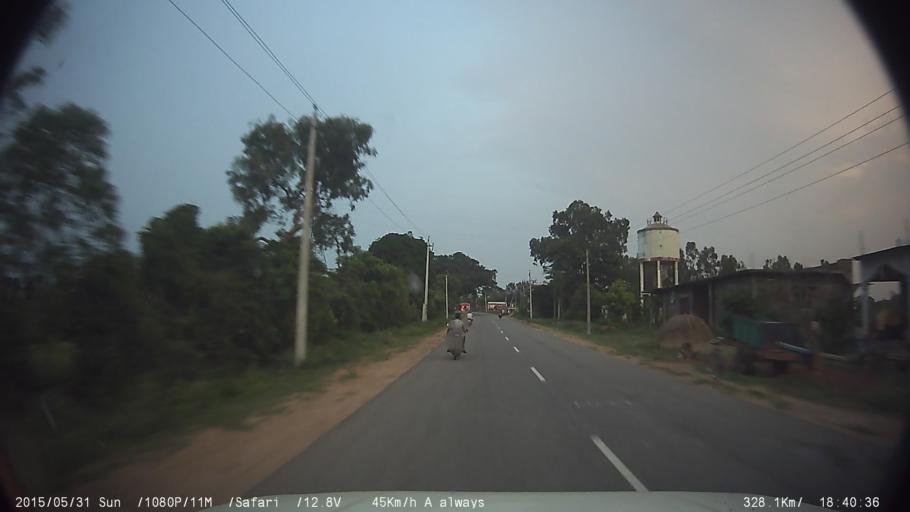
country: IN
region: Karnataka
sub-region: Mysore
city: Nanjangud
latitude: 12.1485
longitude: 76.7870
